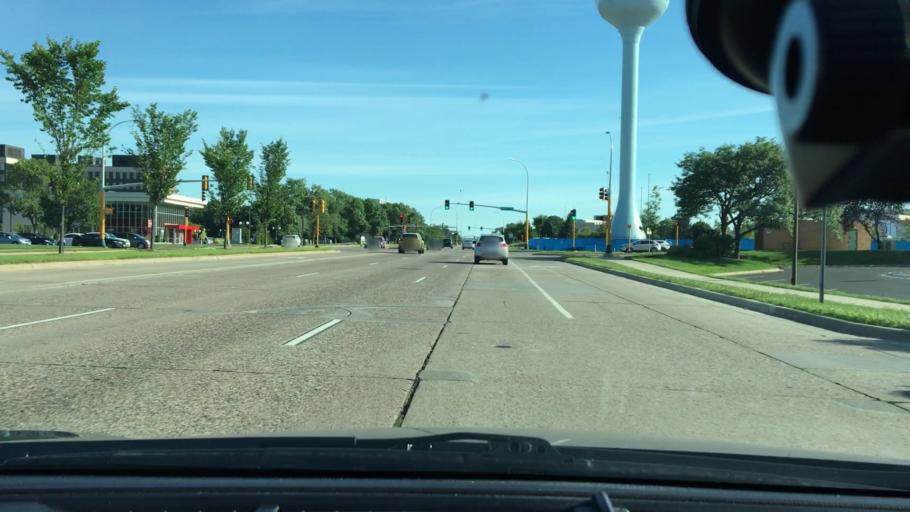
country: US
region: Minnesota
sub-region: Hennepin County
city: Edina
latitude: 44.8774
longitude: -93.3289
